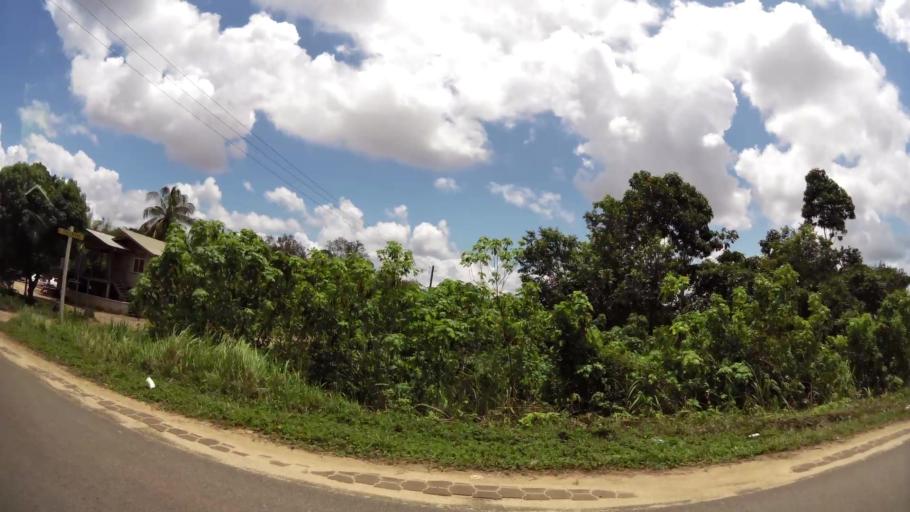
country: SR
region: Paramaribo
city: Paramaribo
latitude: 5.7975
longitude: -55.1375
